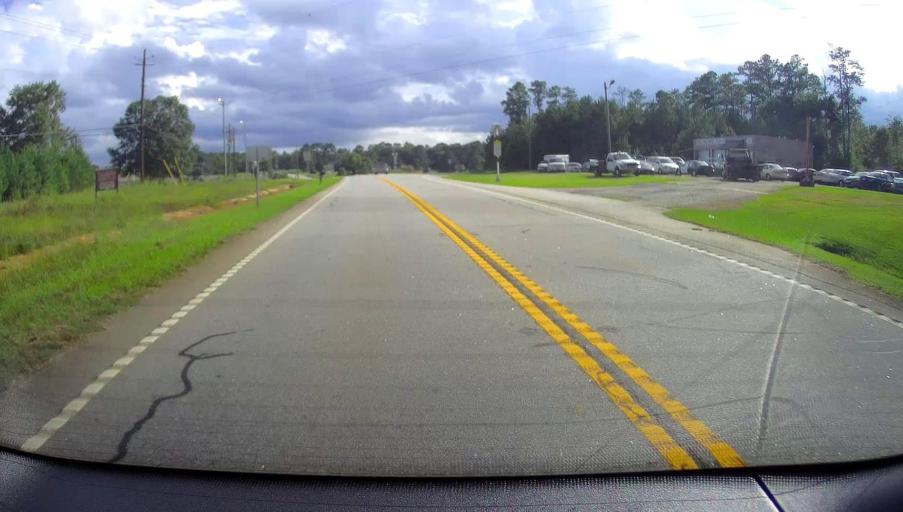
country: US
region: Georgia
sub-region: Meriwether County
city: Manchester
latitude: 32.9961
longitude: -84.5723
